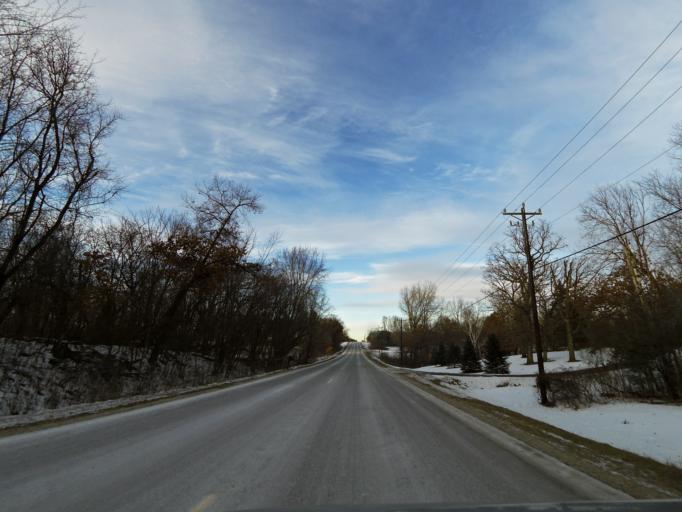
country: US
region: Minnesota
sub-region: Washington County
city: Afton
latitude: 44.9054
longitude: -92.8429
